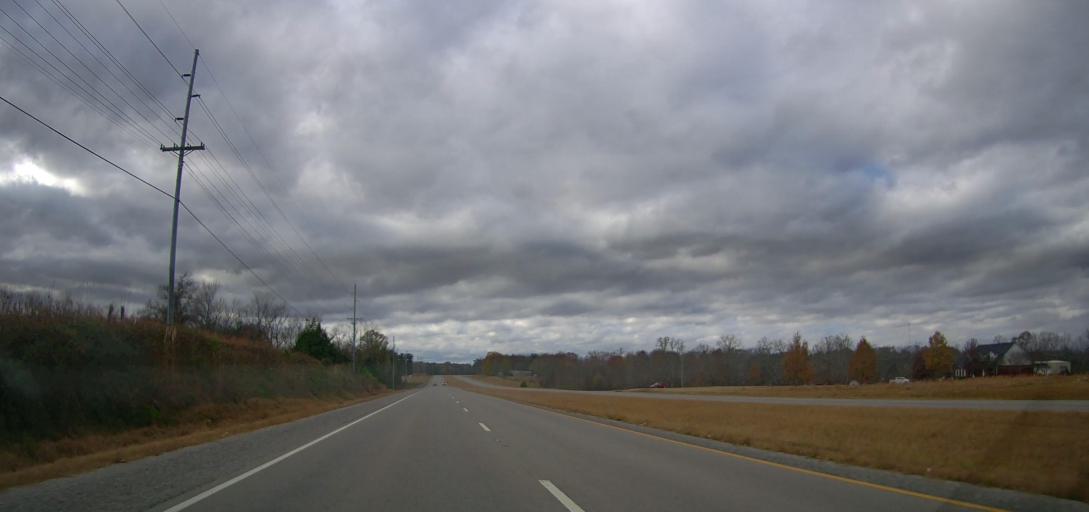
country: US
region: Alabama
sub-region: Lawrence County
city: Town Creek
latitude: 34.5715
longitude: -87.3887
